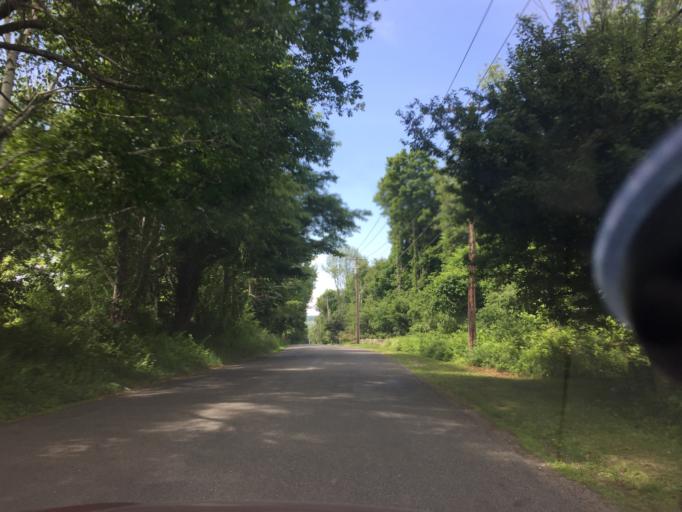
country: US
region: Connecticut
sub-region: Litchfield County
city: Litchfield
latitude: 41.8120
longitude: -73.2620
